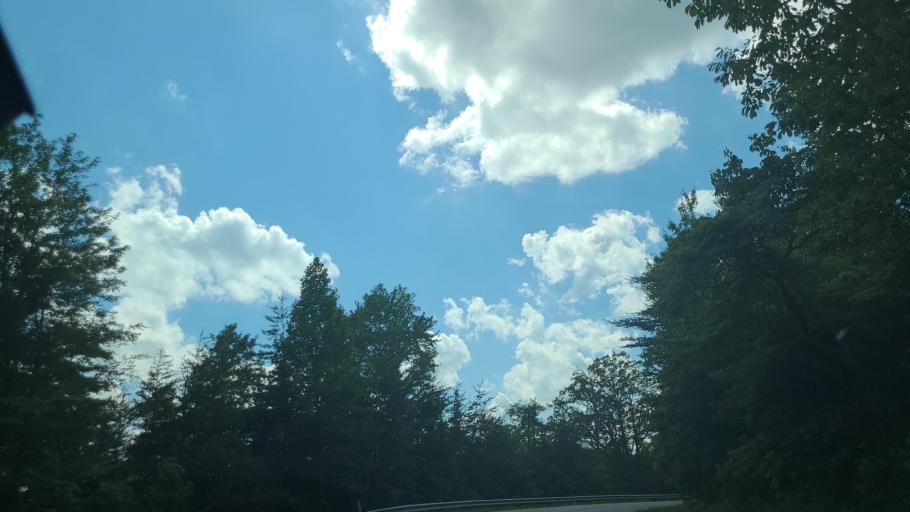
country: US
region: Kentucky
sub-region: Whitley County
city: Williamsburg
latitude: 36.8409
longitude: -84.2942
